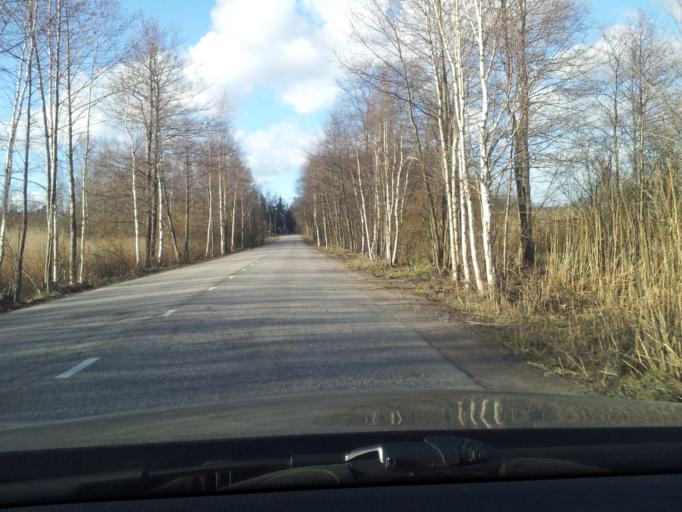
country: FI
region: Uusimaa
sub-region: Helsinki
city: Espoo
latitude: 60.1355
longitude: 24.6819
